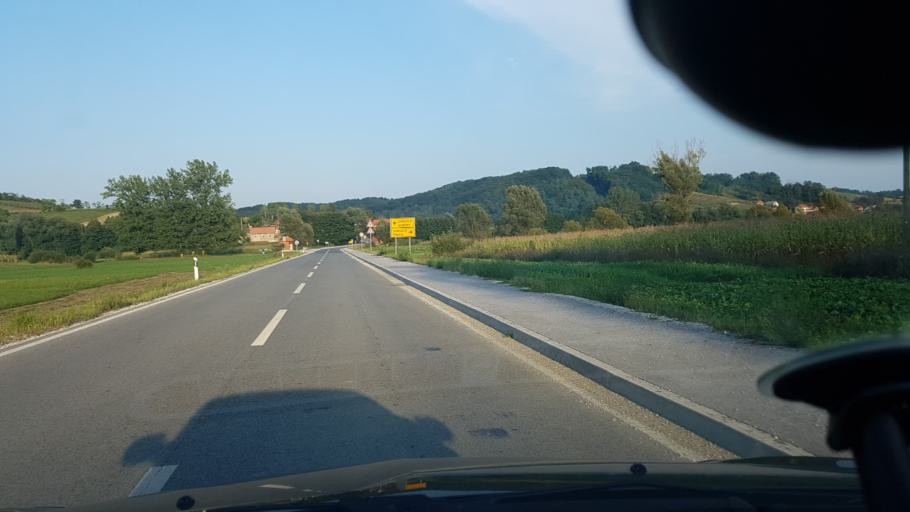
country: HR
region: Krapinsko-Zagorska
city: Pregrada
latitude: 46.1559
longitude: 15.7993
